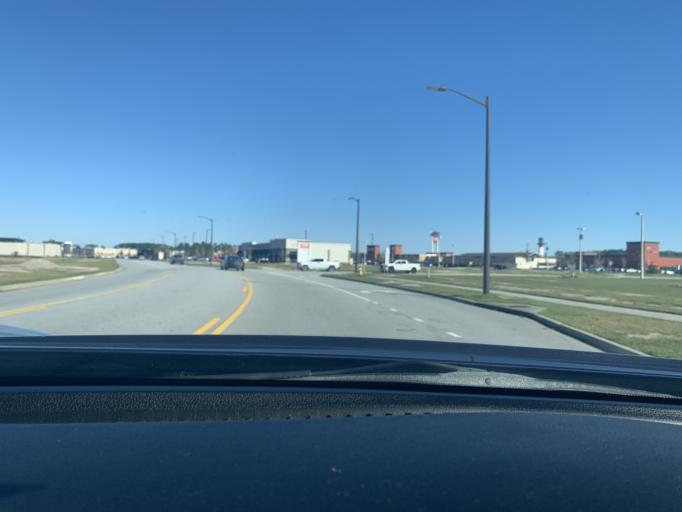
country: US
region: Georgia
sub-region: Chatham County
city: Pooler
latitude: 32.1325
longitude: -81.2474
